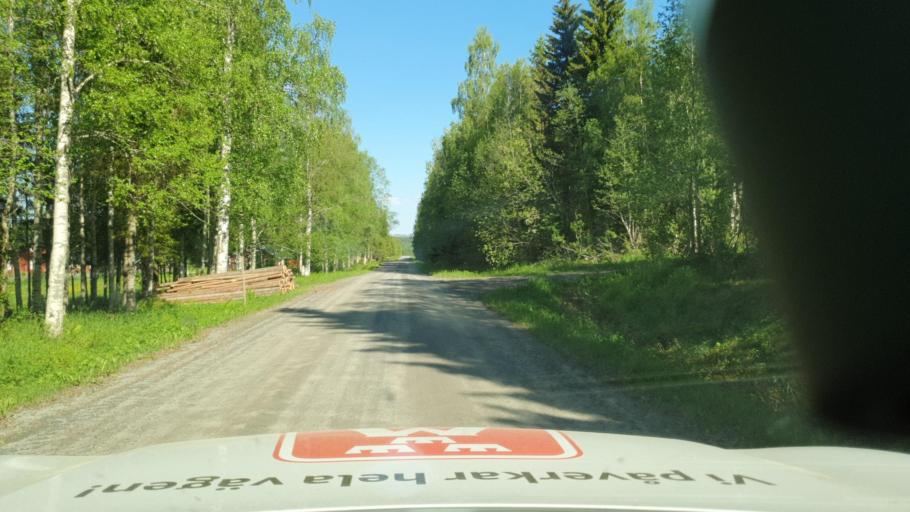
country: SE
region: Vaesterbotten
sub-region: Vannas Kommun
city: Vannasby
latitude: 64.0147
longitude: 19.7672
